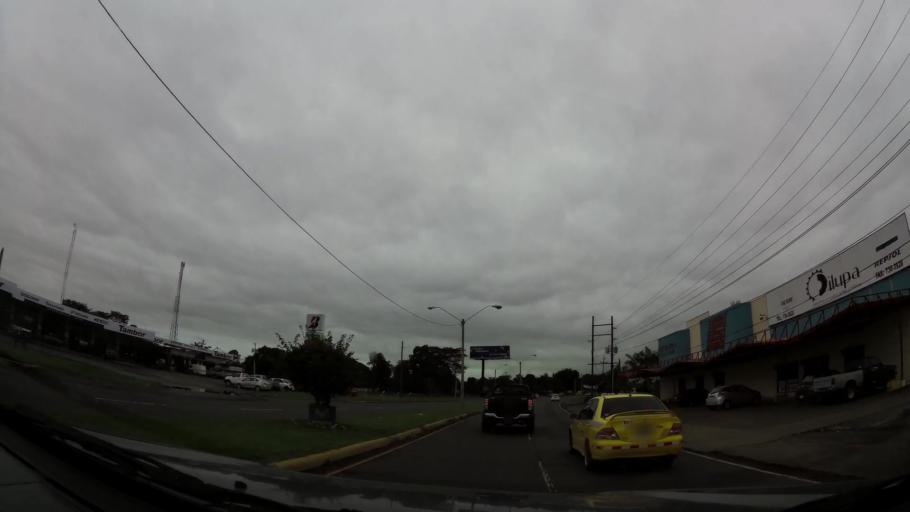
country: PA
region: Chiriqui
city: David
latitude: 8.4299
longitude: -82.4435
